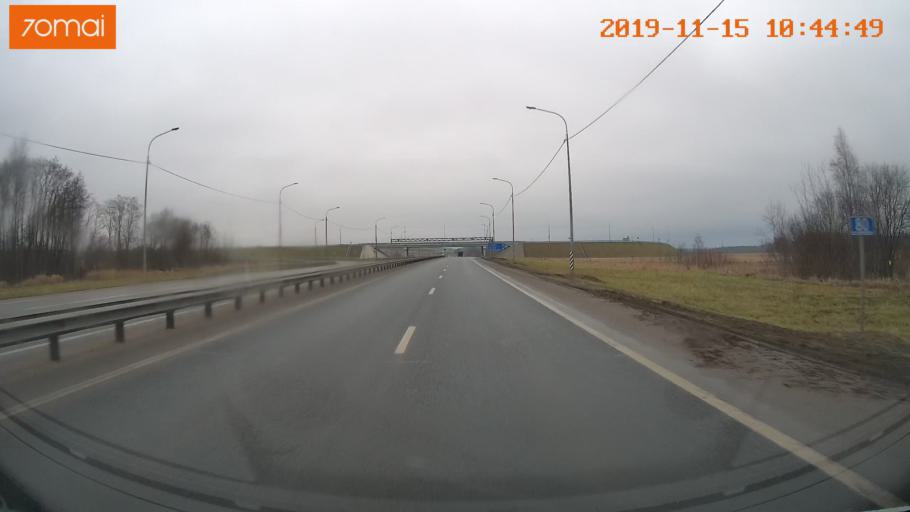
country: RU
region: Vologda
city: Sheksna
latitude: 59.2114
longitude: 38.5688
